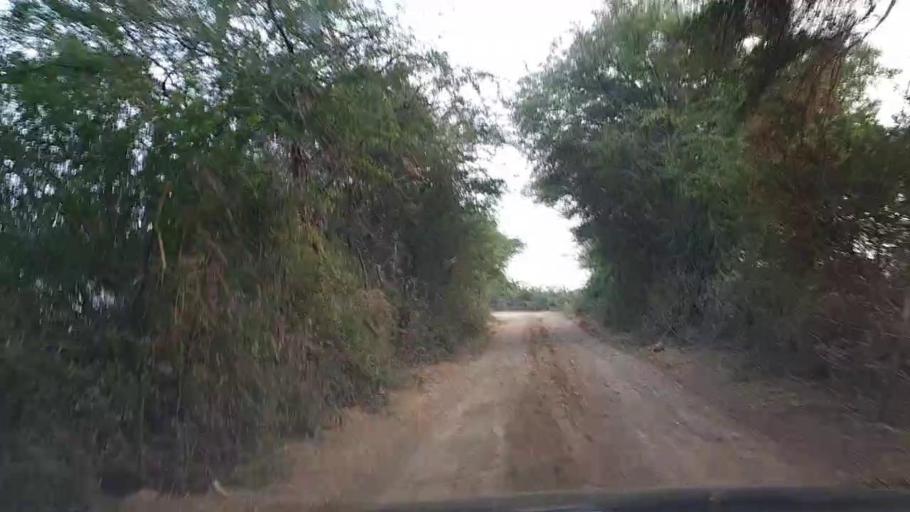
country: PK
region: Sindh
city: Gharo
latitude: 24.7429
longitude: 67.6937
